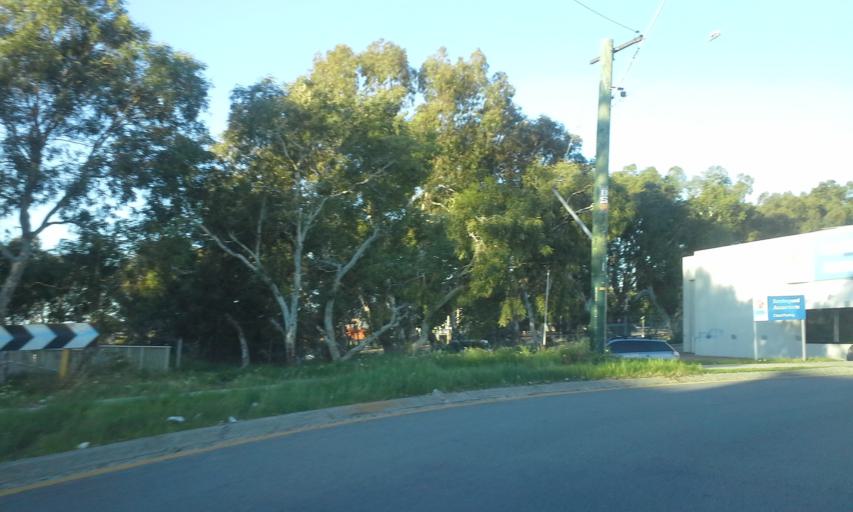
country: AU
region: Western Australia
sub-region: Stirling
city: Osborne Park
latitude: -31.8977
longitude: 115.8127
